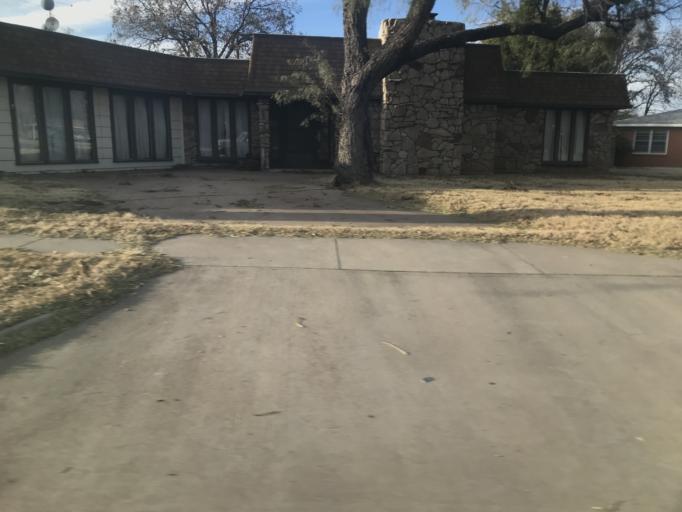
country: US
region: Texas
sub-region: Taylor County
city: Abilene
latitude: 32.4316
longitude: -99.7805
